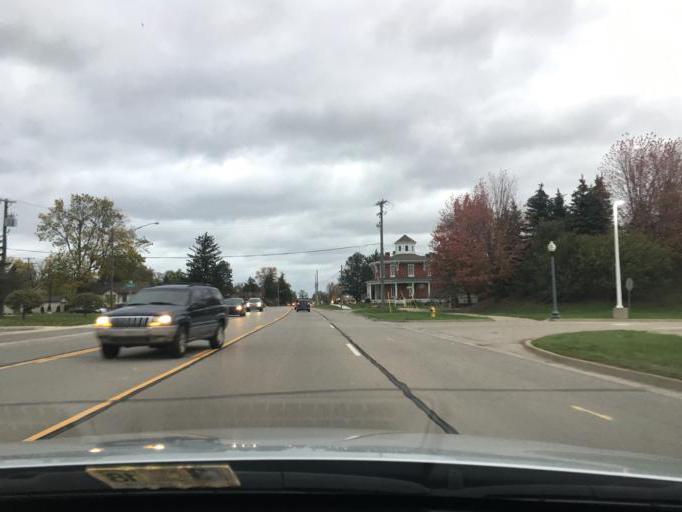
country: US
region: Michigan
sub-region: Macomb County
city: Shelby
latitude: 42.7162
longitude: -83.0354
